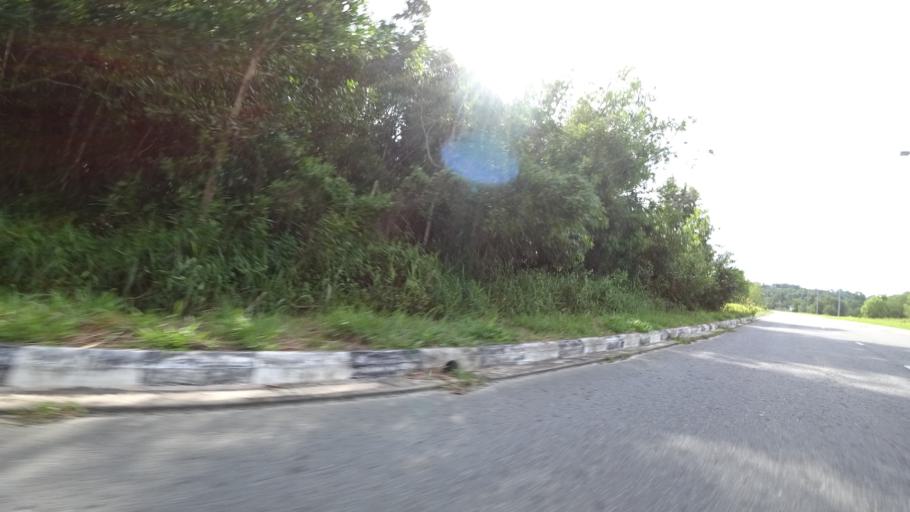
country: BN
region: Brunei and Muara
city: Bandar Seri Begawan
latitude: 4.9003
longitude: 114.8012
